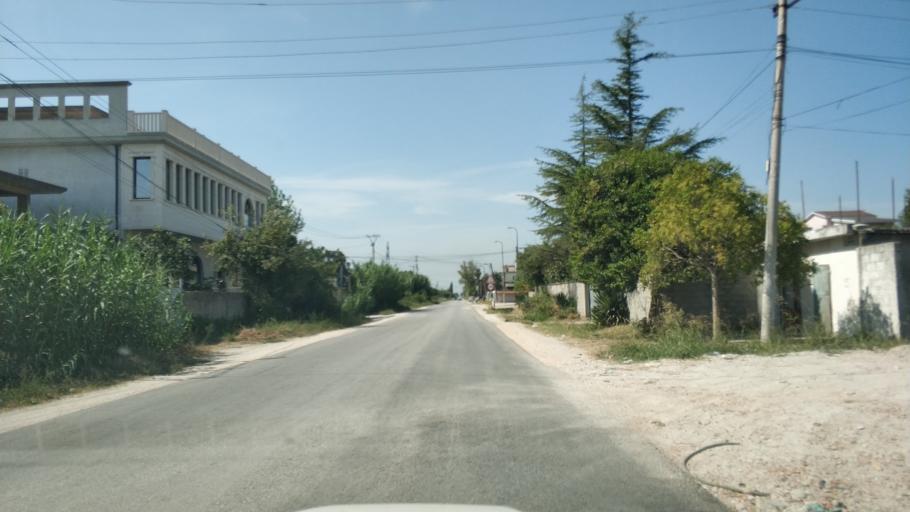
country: AL
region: Fier
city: Fier
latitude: 40.7296
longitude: 19.5439
